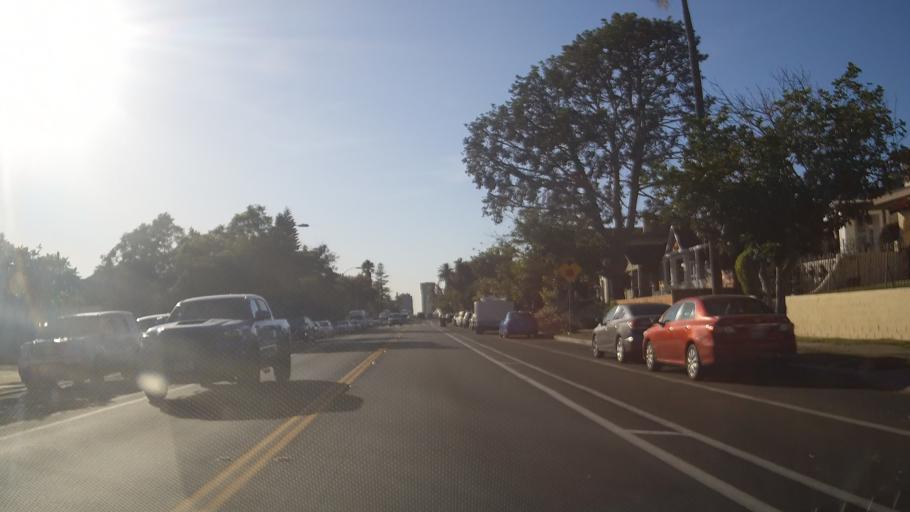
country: US
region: California
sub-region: San Diego County
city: San Diego
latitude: 32.7179
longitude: -117.1367
